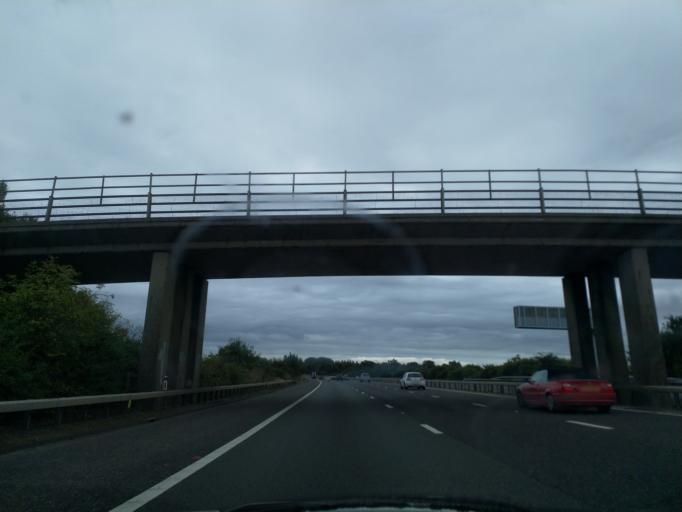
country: GB
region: England
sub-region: Surrey
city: Chertsey
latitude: 51.3964
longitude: -0.5006
